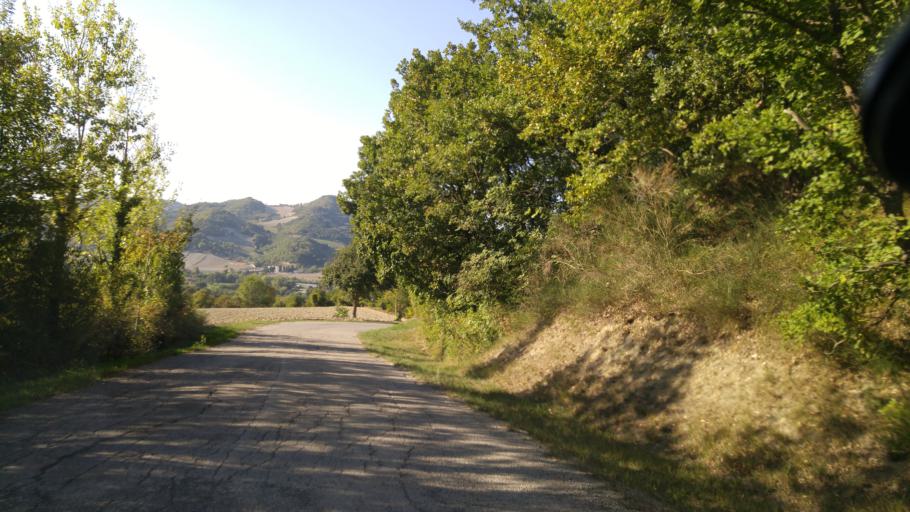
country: IT
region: The Marches
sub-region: Provincia di Pesaro e Urbino
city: Fermignano
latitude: 43.6627
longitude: 12.6498
